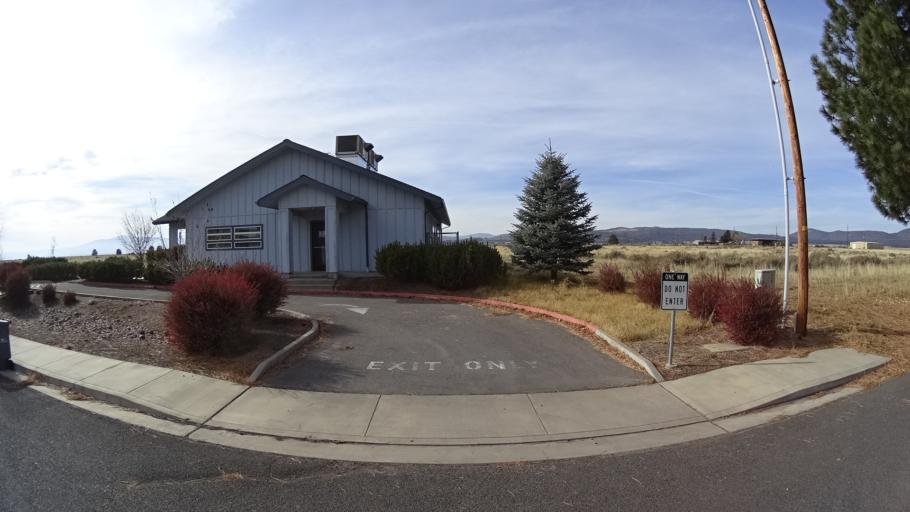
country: US
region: Oregon
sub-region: Klamath County
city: Klamath Falls
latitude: 41.9647
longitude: -121.9267
